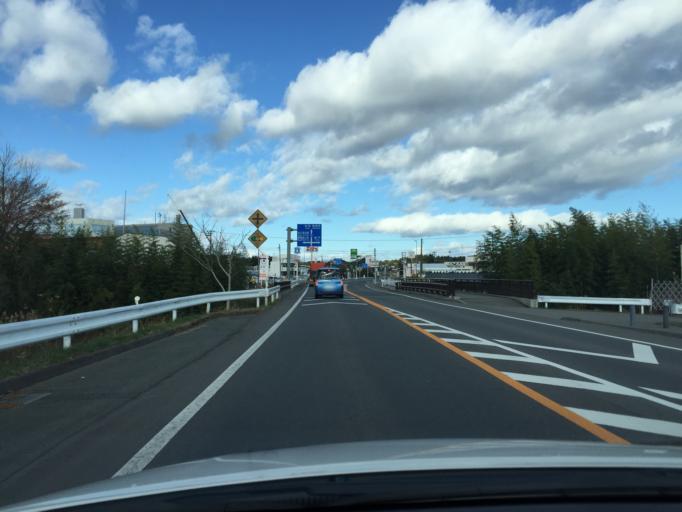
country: JP
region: Fukushima
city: Namie
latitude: 37.4927
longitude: 141.0029
